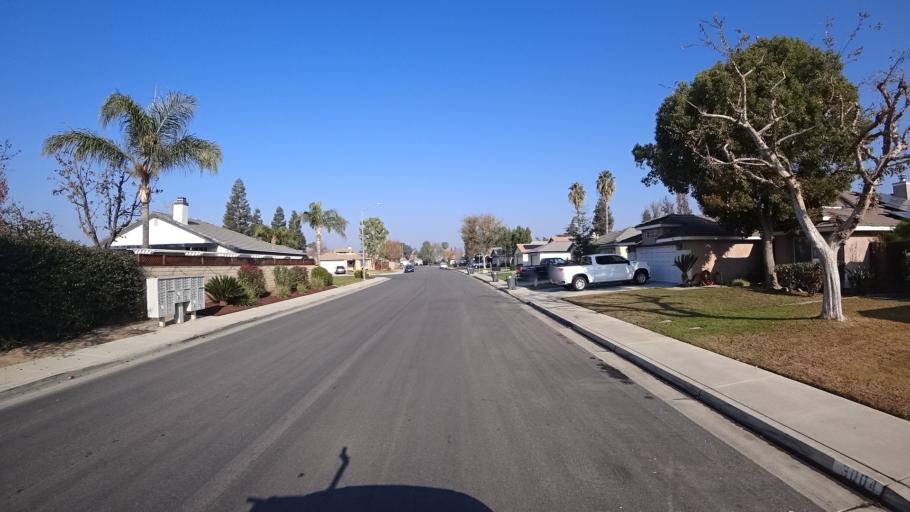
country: US
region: California
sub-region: Kern County
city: Greenacres
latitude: 35.3883
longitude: -119.1017
